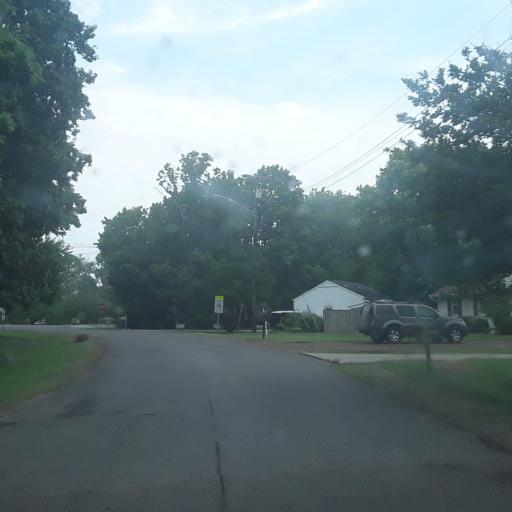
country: US
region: Tennessee
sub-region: Williamson County
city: Brentwood
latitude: 36.0602
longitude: -86.7209
